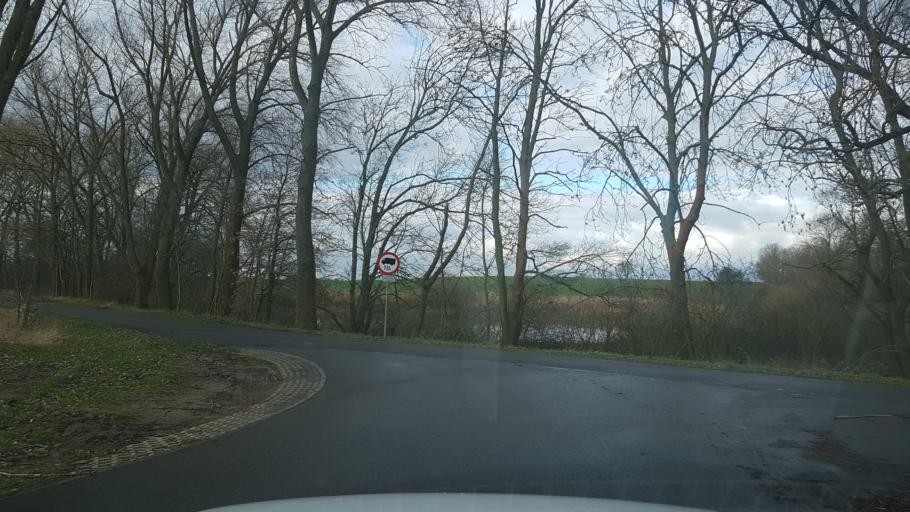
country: PL
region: West Pomeranian Voivodeship
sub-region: Powiat policki
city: Kolbaskowo
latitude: 53.3833
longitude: 14.4033
